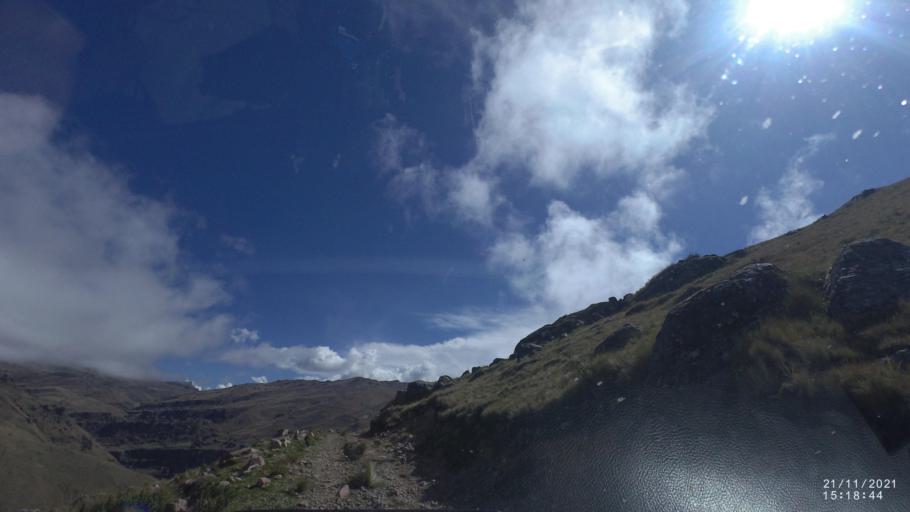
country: BO
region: Cochabamba
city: Cochabamba
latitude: -16.9577
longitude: -66.2632
